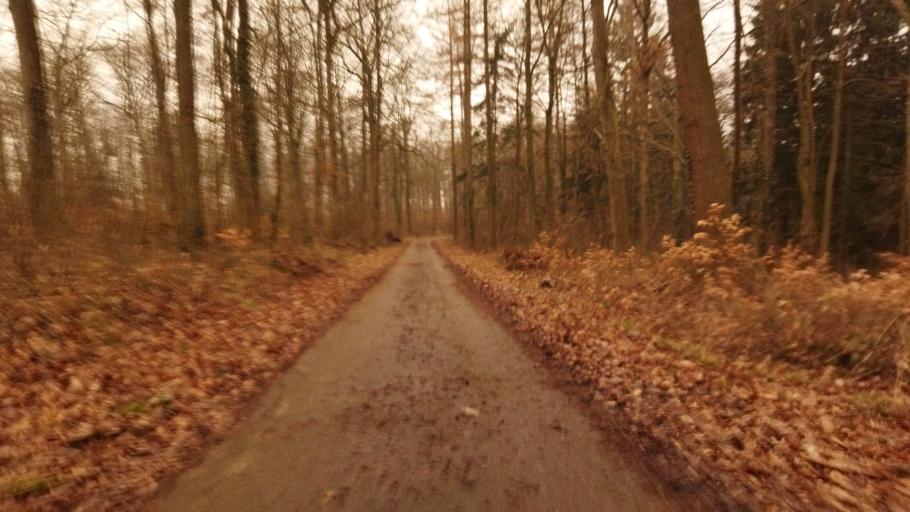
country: DE
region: Baden-Wuerttemberg
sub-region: Regierungsbezirk Stuttgart
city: Erlenbach
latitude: 49.1482
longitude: 9.2582
